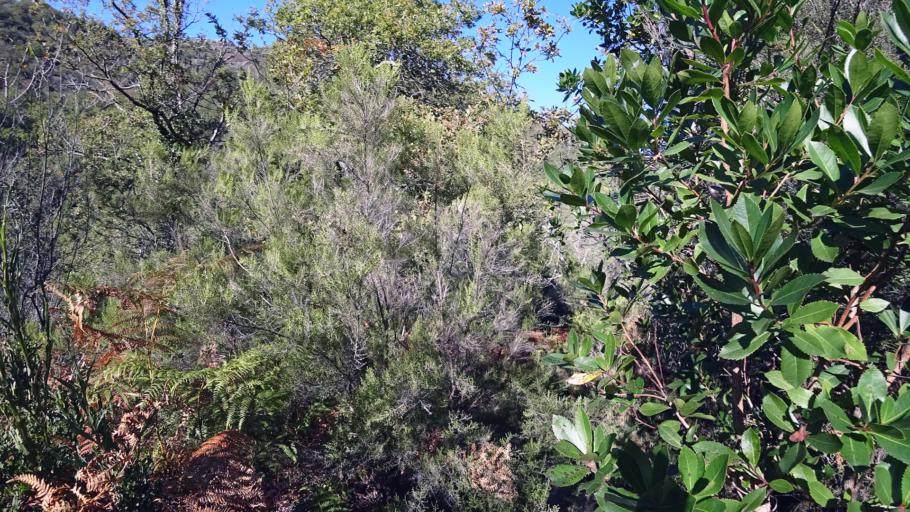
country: ES
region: Galicia
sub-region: Provincia de Ourense
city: Lobios
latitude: 41.7990
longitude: -8.1506
